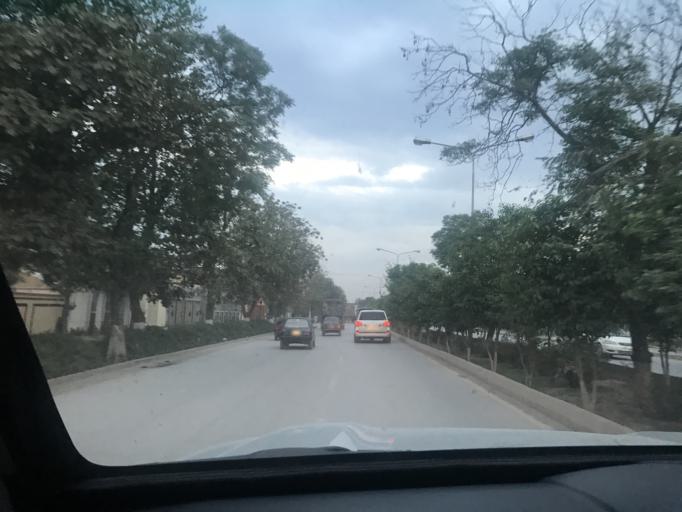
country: PK
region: Khyber Pakhtunkhwa
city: Peshawar
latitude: 33.9772
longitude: 71.4485
